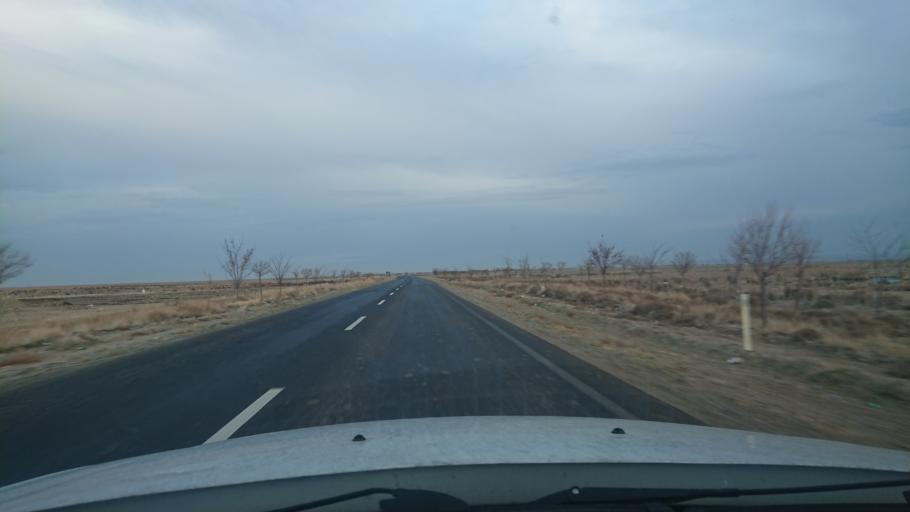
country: TR
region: Aksaray
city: Yesilova
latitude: 38.3081
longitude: 33.7546
